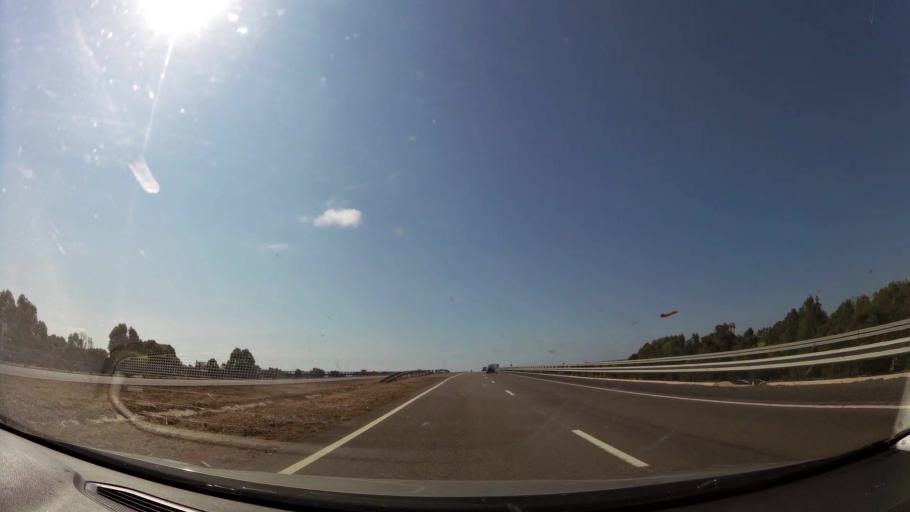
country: MA
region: Rabat-Sale-Zemmour-Zaer
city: Skhirat
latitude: 33.8706
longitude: -7.0012
